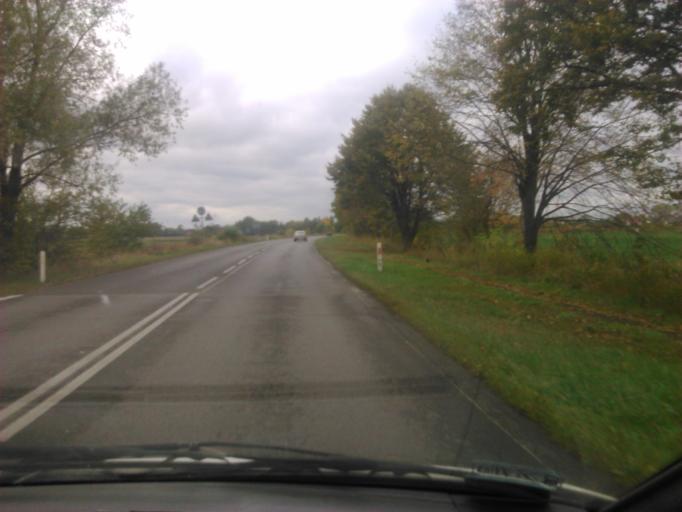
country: PL
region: Pomeranian Voivodeship
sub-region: Powiat gdanski
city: Cedry Wielkie
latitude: 54.3301
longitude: 18.7984
